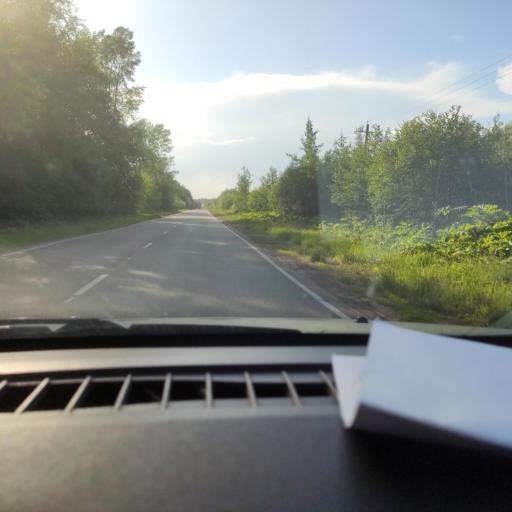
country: RU
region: Perm
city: Krasnokamsk
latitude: 58.1256
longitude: 55.8027
